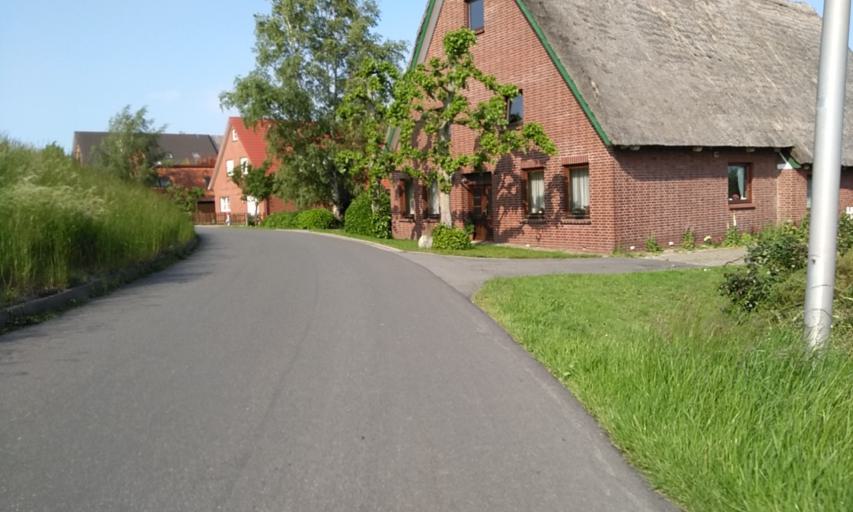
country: DE
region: Lower Saxony
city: Buxtehude
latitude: 53.4988
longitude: 9.7265
